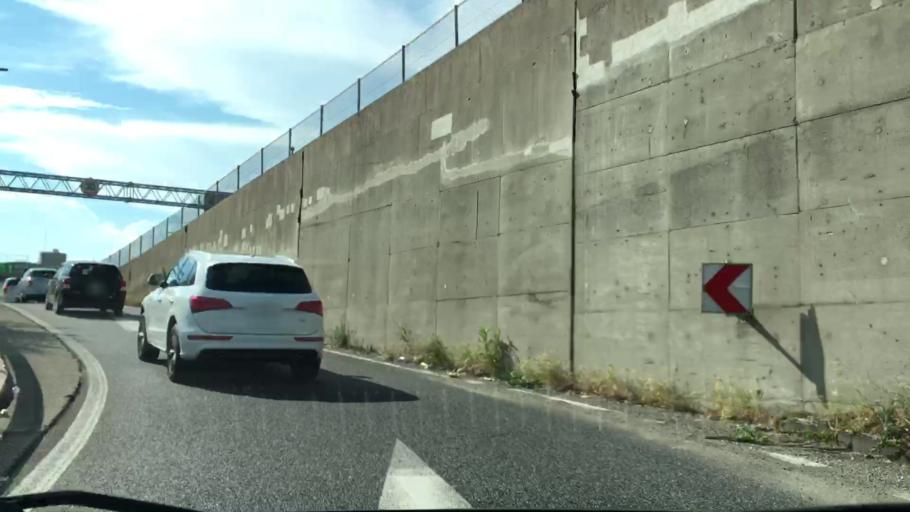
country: JP
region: Hyogo
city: Akashi
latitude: 34.6856
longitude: 134.9823
